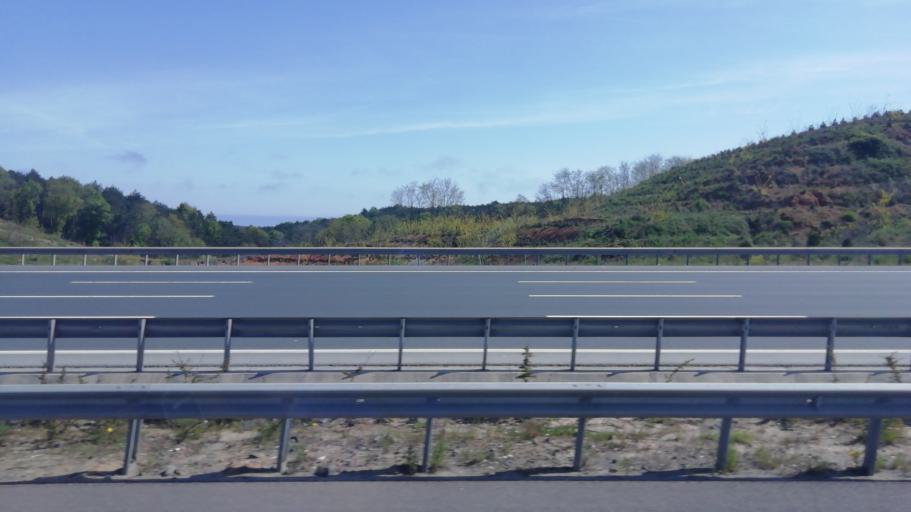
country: TR
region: Istanbul
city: Arikoey
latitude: 41.2216
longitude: 29.0806
